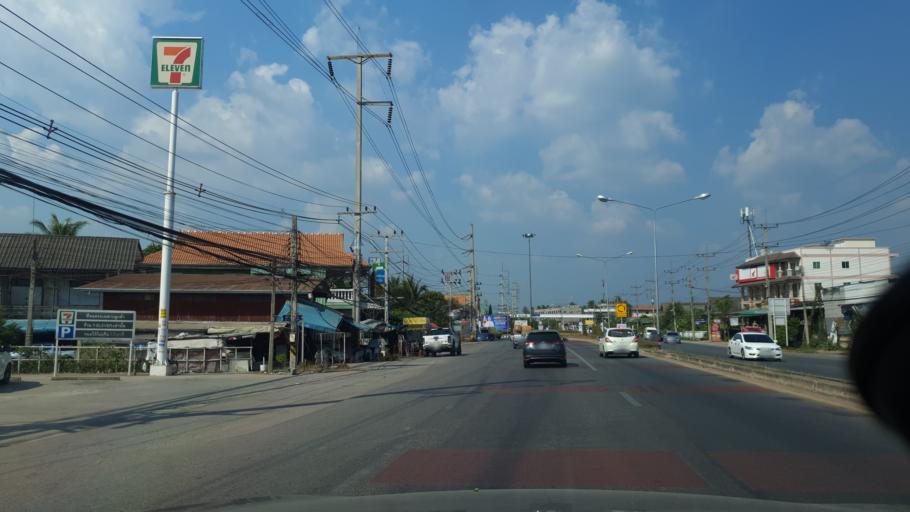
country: TH
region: Samut Songkhram
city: Amphawa
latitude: 13.4178
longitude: 99.9636
